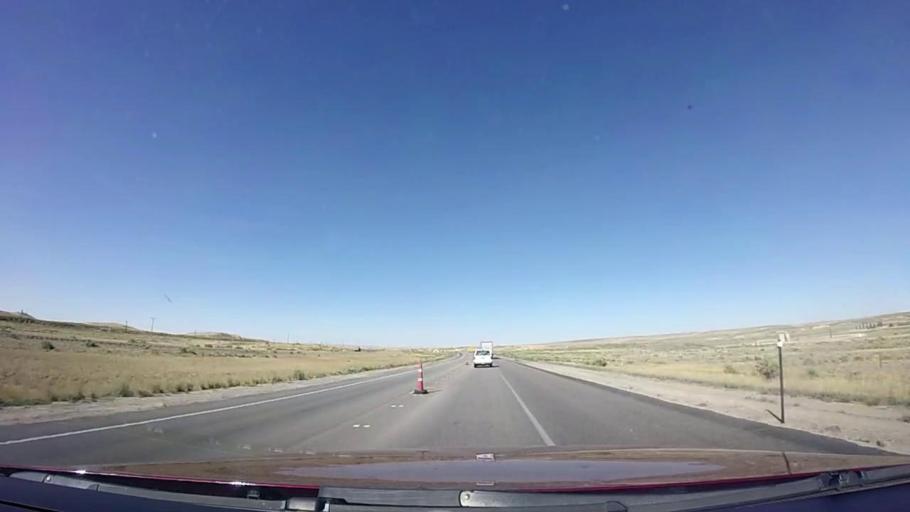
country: US
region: Wyoming
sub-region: Carbon County
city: Rawlins
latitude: 41.7049
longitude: -107.8942
